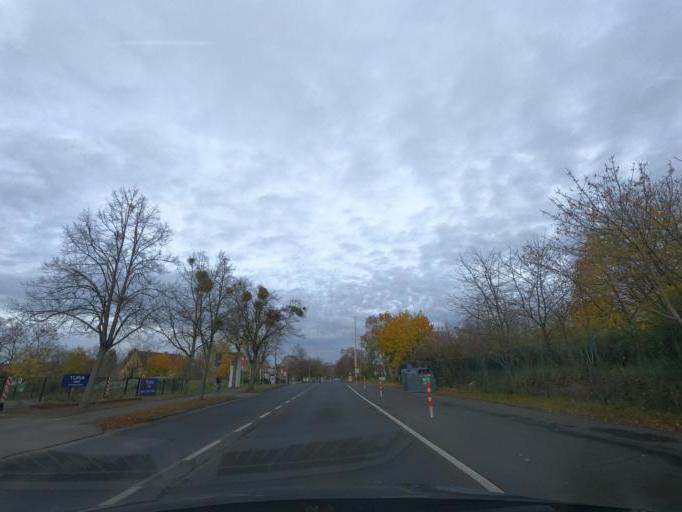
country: DE
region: Lower Saxony
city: Braunschweig
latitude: 52.2931
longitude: 10.5400
